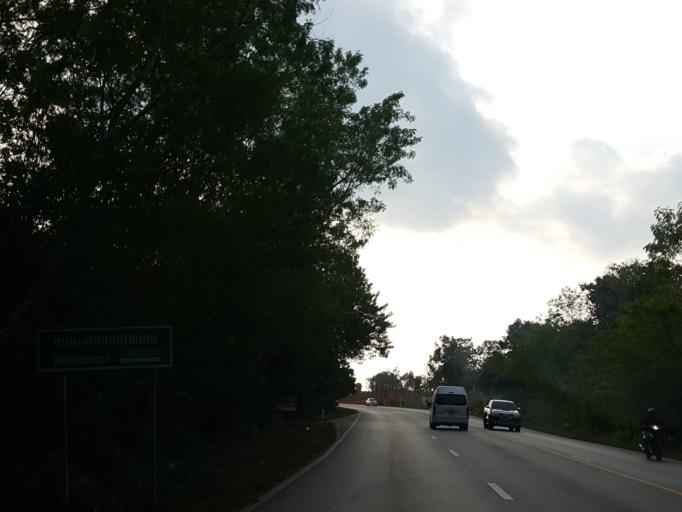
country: TH
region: Chiang Mai
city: Mae On
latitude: 18.9157
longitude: 99.2309
